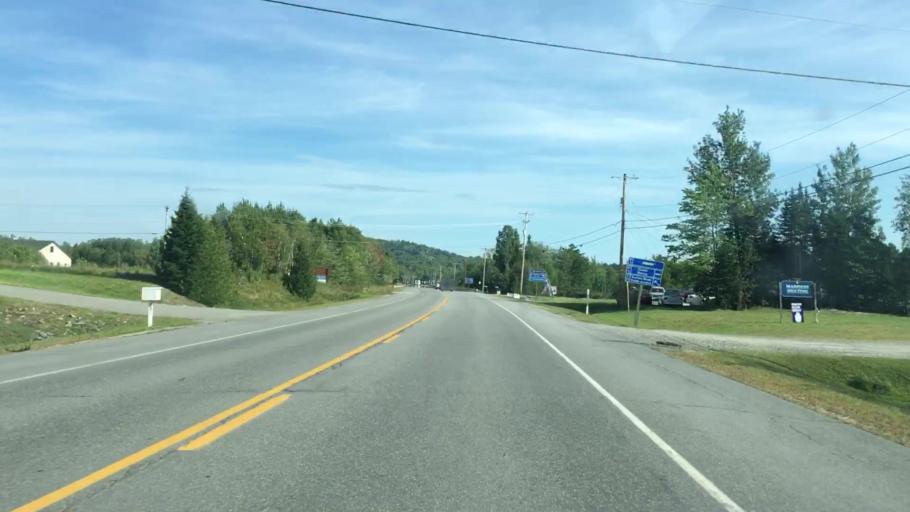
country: US
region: Maine
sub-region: Penobscot County
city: Lincoln
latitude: 45.3572
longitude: -68.5407
